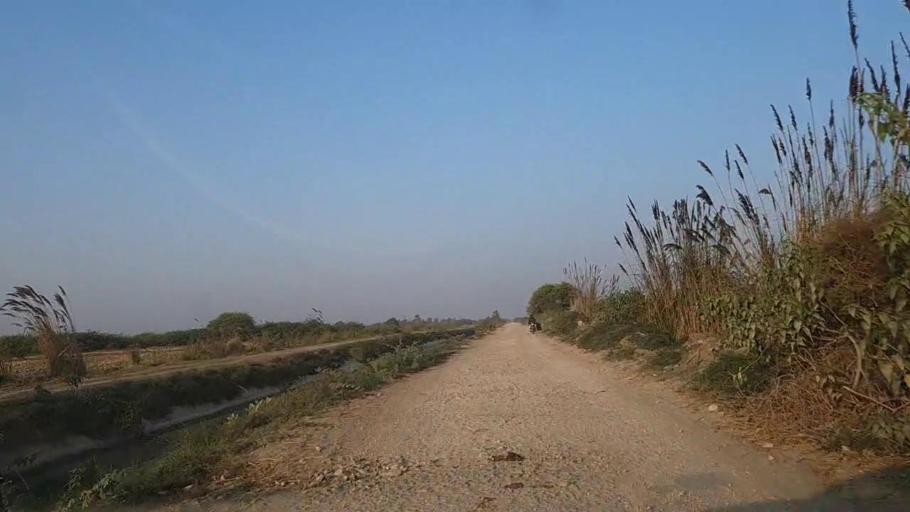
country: PK
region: Sindh
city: Keti Bandar
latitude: 24.2795
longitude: 67.6862
